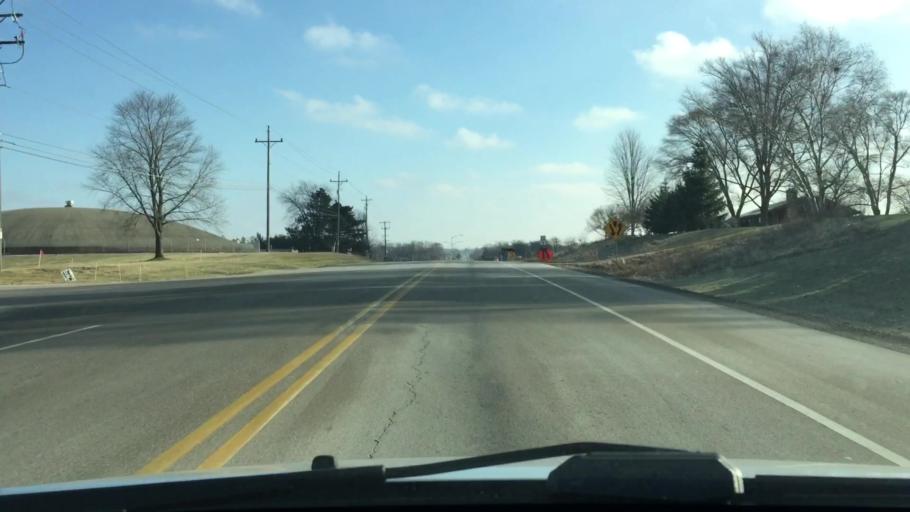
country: US
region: Wisconsin
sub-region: Waukesha County
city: Waukesha
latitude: 42.9885
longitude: -88.2708
